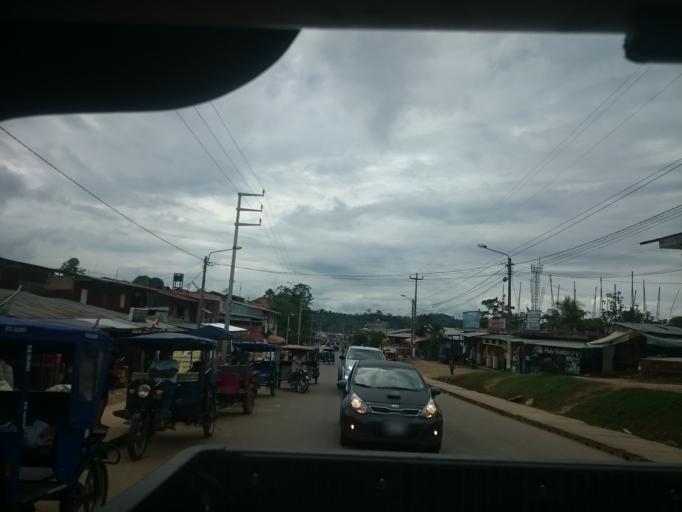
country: PE
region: Huanuco
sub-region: Puerto Inca
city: Tournavista
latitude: -8.8300
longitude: -75.2173
